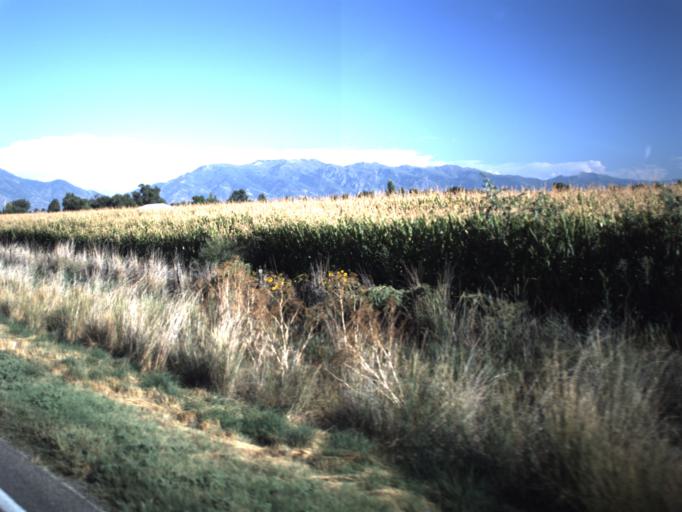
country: US
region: Utah
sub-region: Weber County
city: Hooper
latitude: 41.1907
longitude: -112.1203
